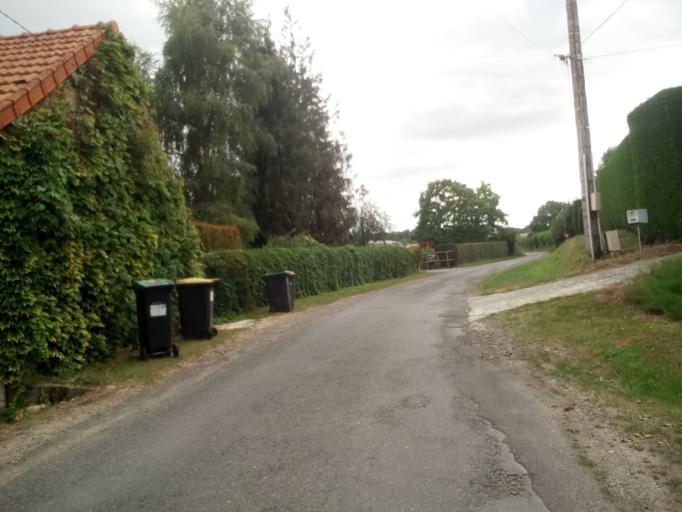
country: FR
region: Lower Normandy
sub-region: Departement du Calvados
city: Troarn
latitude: 49.1596
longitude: -0.1539
